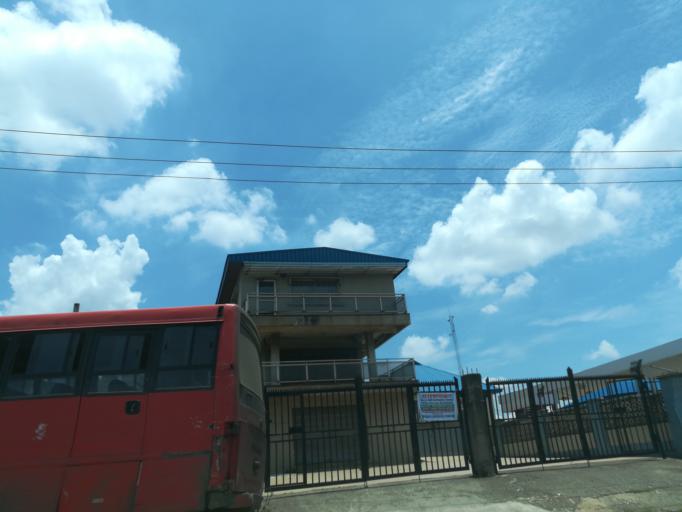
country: NG
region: Lagos
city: Ikorodu
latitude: 6.6133
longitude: 3.5014
